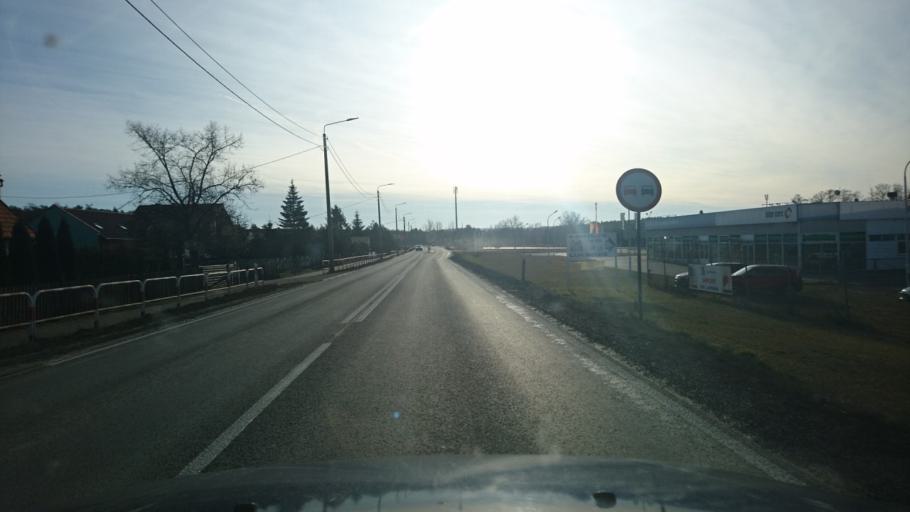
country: PL
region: Greater Poland Voivodeship
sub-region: Powiat ostrzeszowski
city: Ostrzeszow
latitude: 51.4387
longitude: 17.9146
